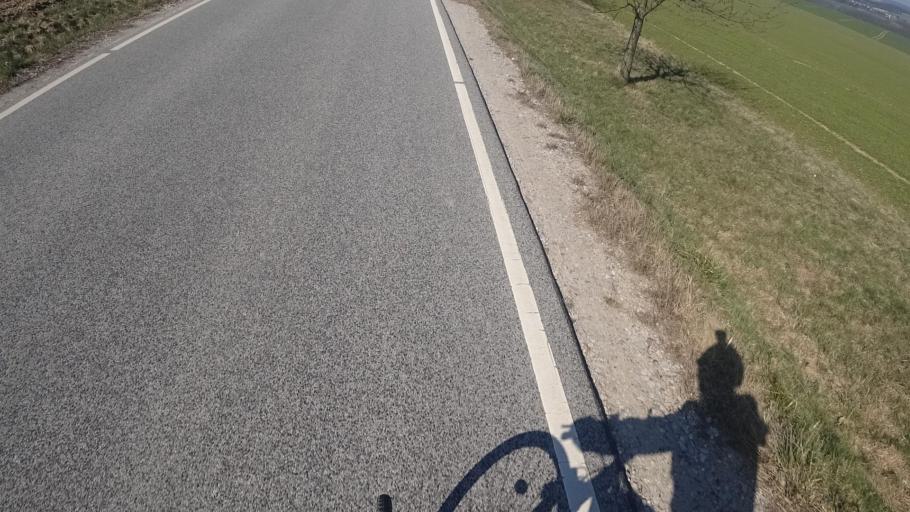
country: DE
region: Rheinland-Pfalz
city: Mengerschied
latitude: 49.9244
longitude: 7.4999
